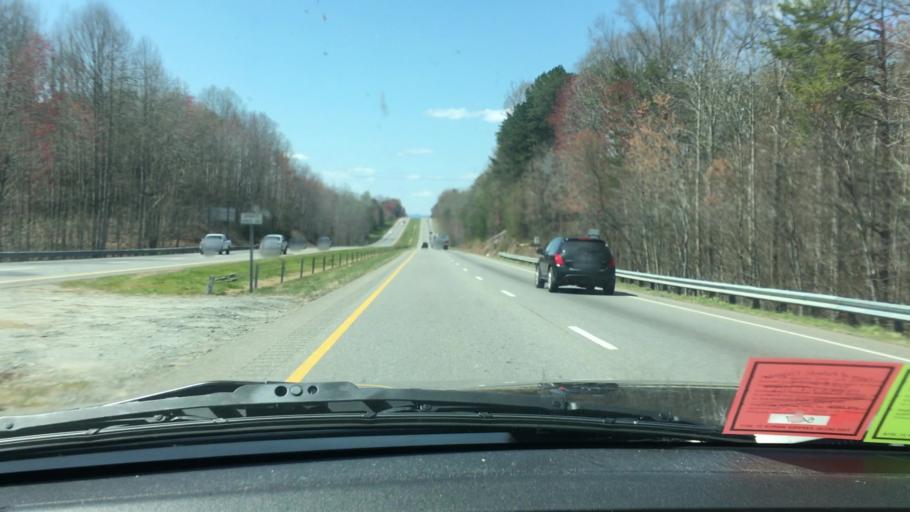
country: US
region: North Carolina
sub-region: Surry County
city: Pilot Mountain
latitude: 36.4119
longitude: -80.5035
